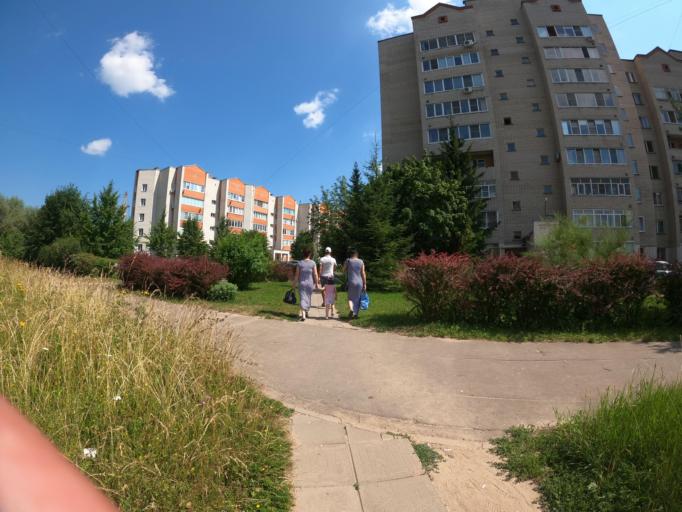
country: RU
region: Kaluga
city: Obninsk
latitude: 55.1161
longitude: 36.5849
